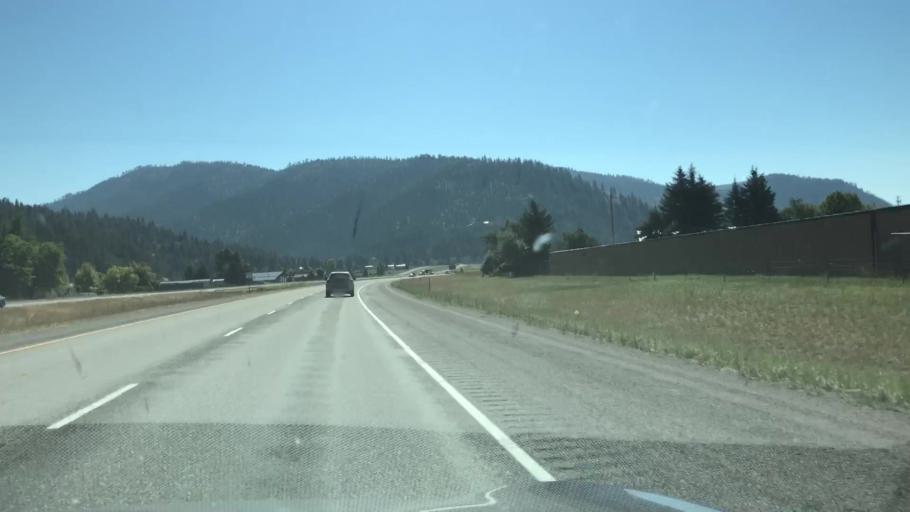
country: US
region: Montana
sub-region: Missoula County
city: Clinton
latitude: 46.7853
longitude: -113.7241
